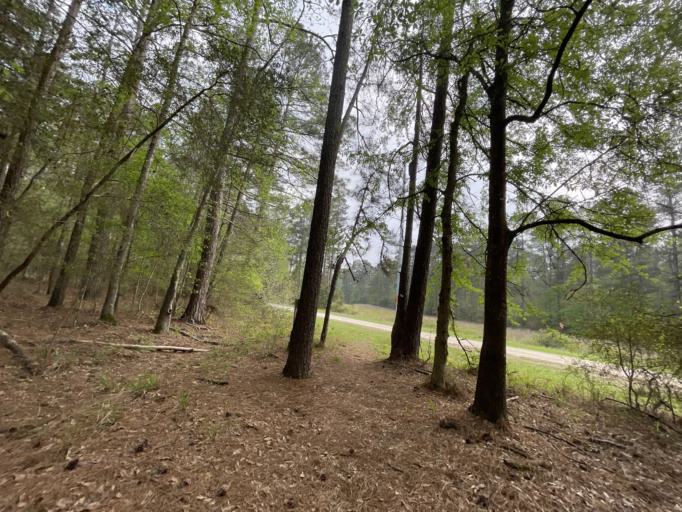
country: US
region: Texas
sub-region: Walker County
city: Huntsville
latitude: 30.6513
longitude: -95.4844
